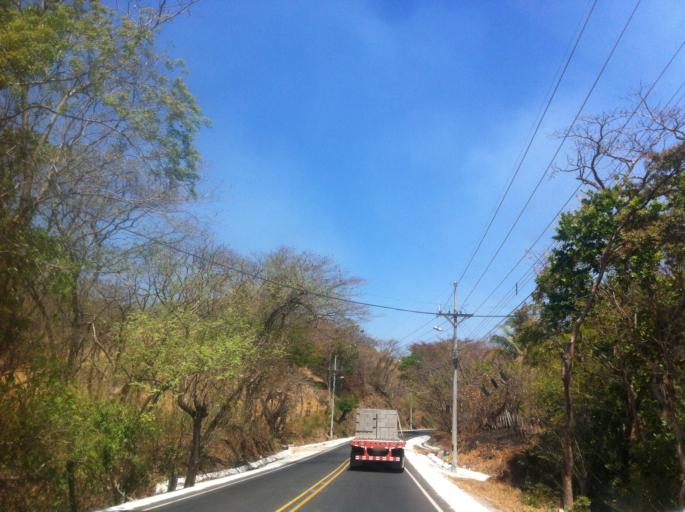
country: CR
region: Guanacaste
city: Santa Cruz
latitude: 10.2146
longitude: -85.5118
